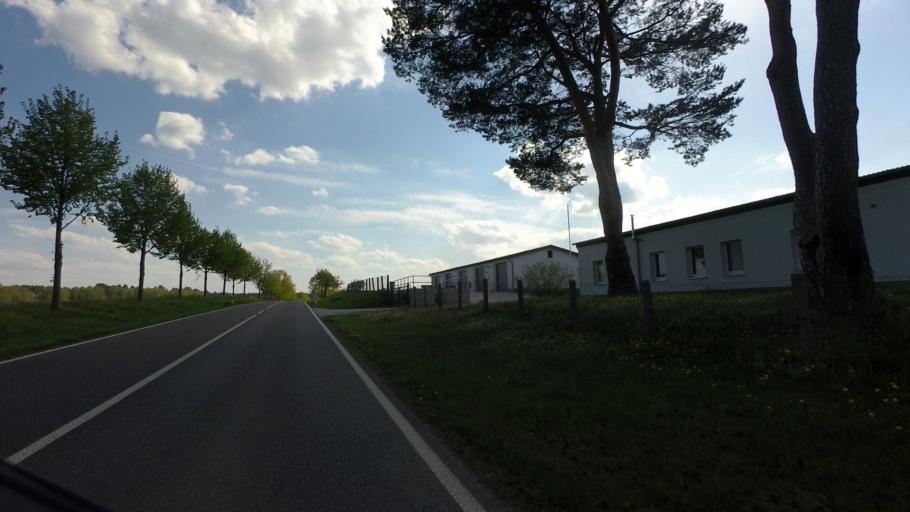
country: DE
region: Brandenburg
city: Templin
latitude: 53.1038
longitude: 13.5009
